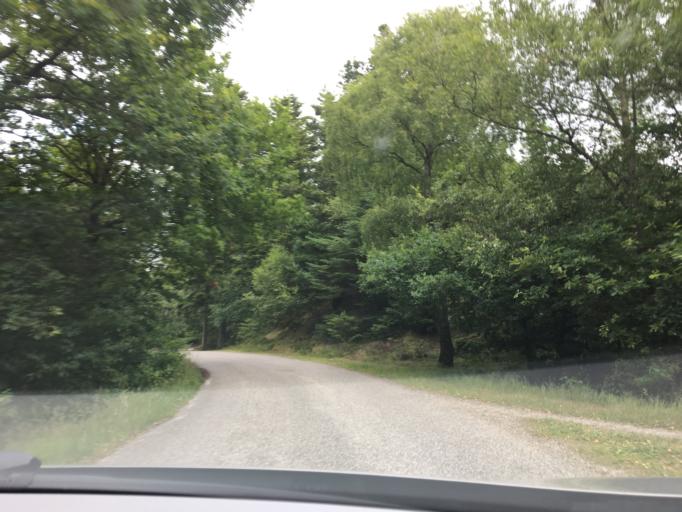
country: DK
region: South Denmark
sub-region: Varde Kommune
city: Oksbol
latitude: 55.7491
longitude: 8.2435
